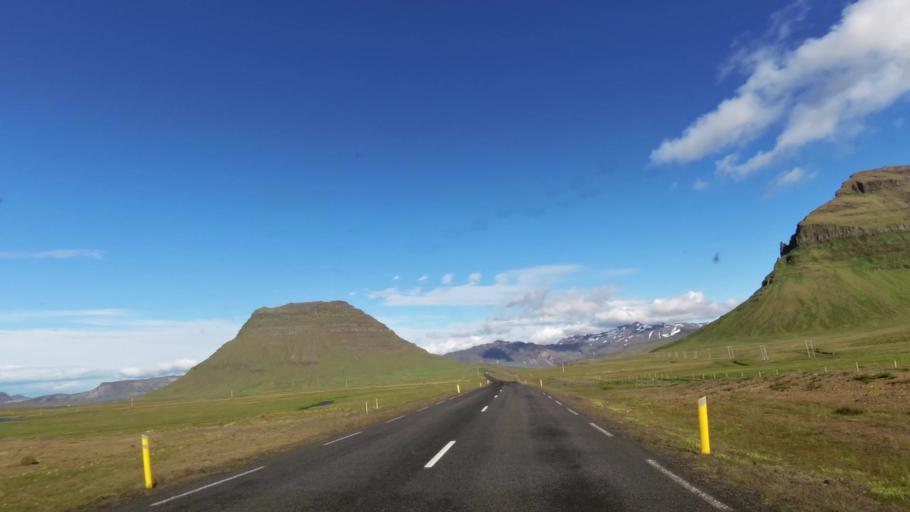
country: IS
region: West
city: Olafsvik
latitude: 64.9416
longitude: -23.3767
